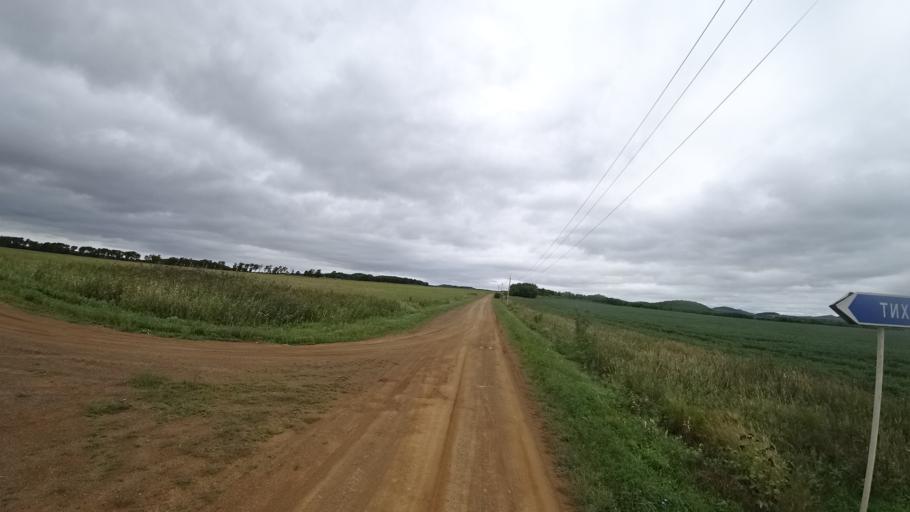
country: RU
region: Primorskiy
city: Chernigovka
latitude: 44.4349
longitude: 132.5924
